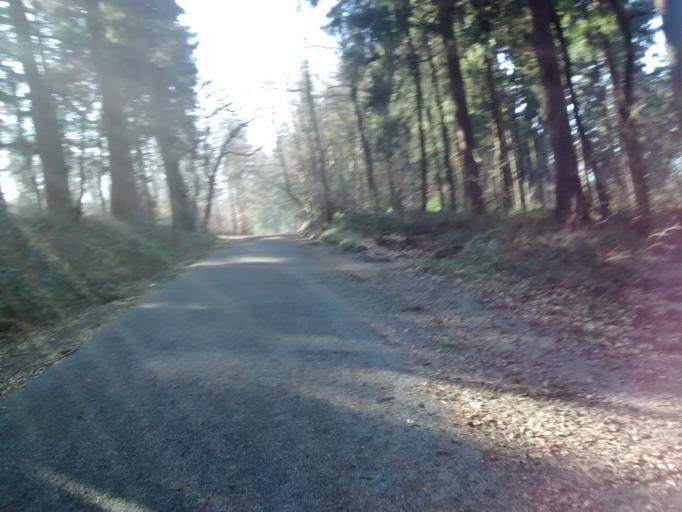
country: NL
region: Limburg
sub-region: Gemeente Vaals
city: Vaals
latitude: 50.7496
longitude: 6.0448
